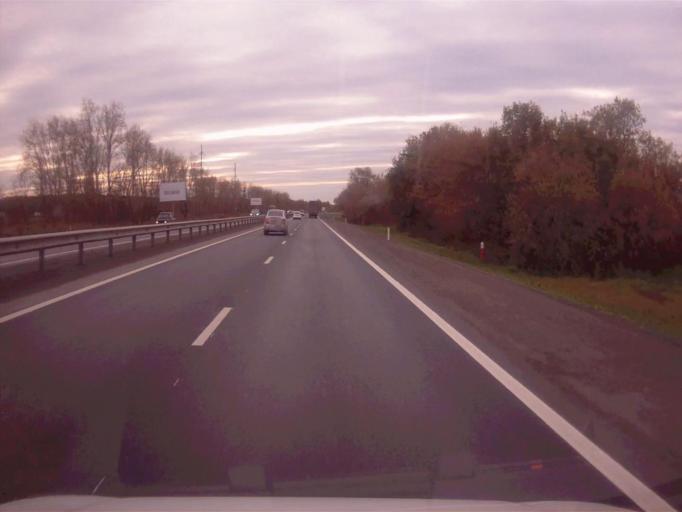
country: RU
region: Chelyabinsk
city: Roza
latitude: 54.9863
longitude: 61.4351
